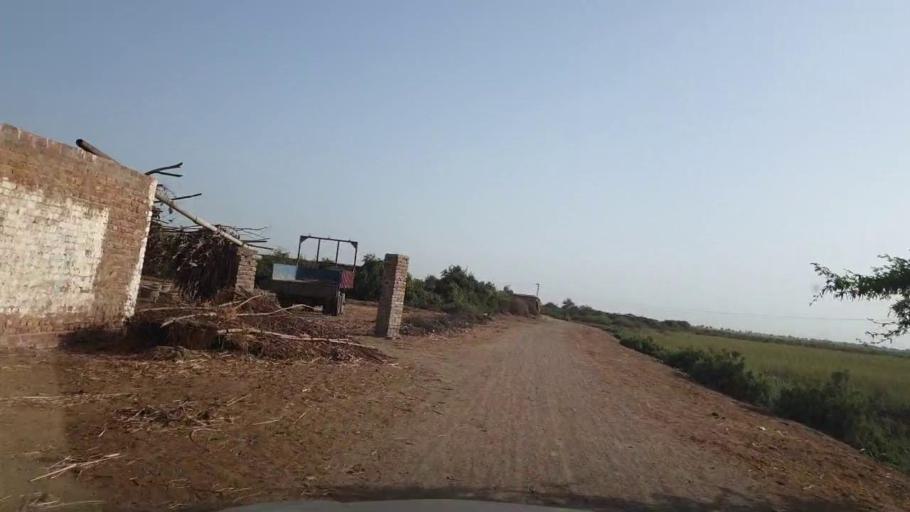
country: PK
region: Sindh
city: Tando Ghulam Ali
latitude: 25.0690
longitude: 68.8918
